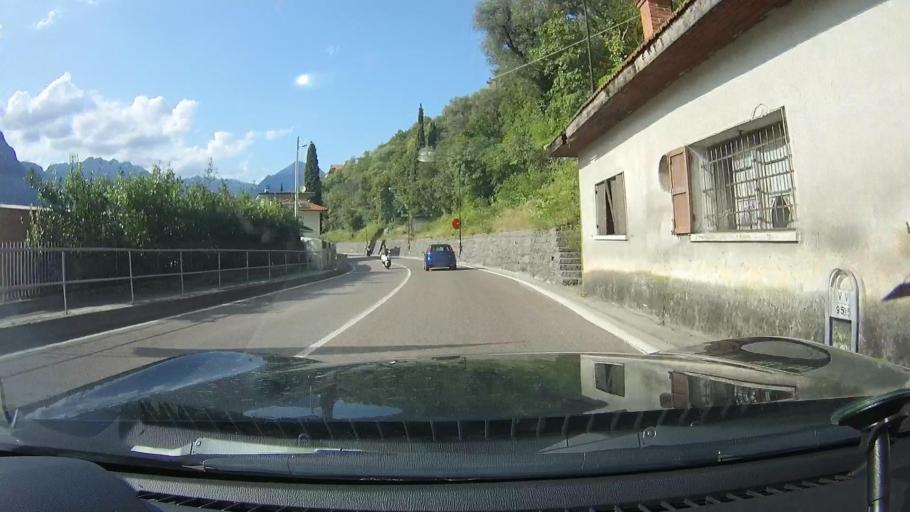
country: IT
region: Trentino-Alto Adige
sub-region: Provincia di Trento
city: Torbole sul Garda
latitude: 45.8625
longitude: 10.8767
